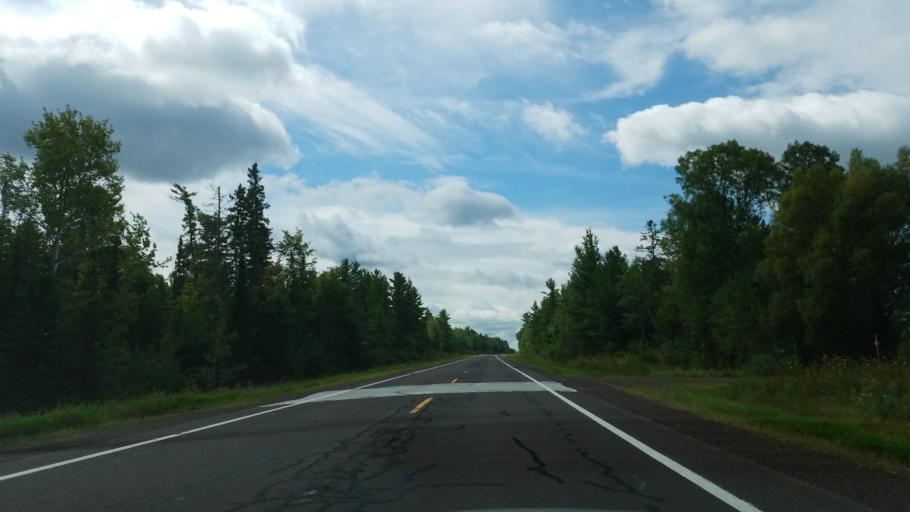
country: US
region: Michigan
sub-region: Ontonagon County
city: Ontonagon
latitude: 46.6553
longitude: -89.1733
